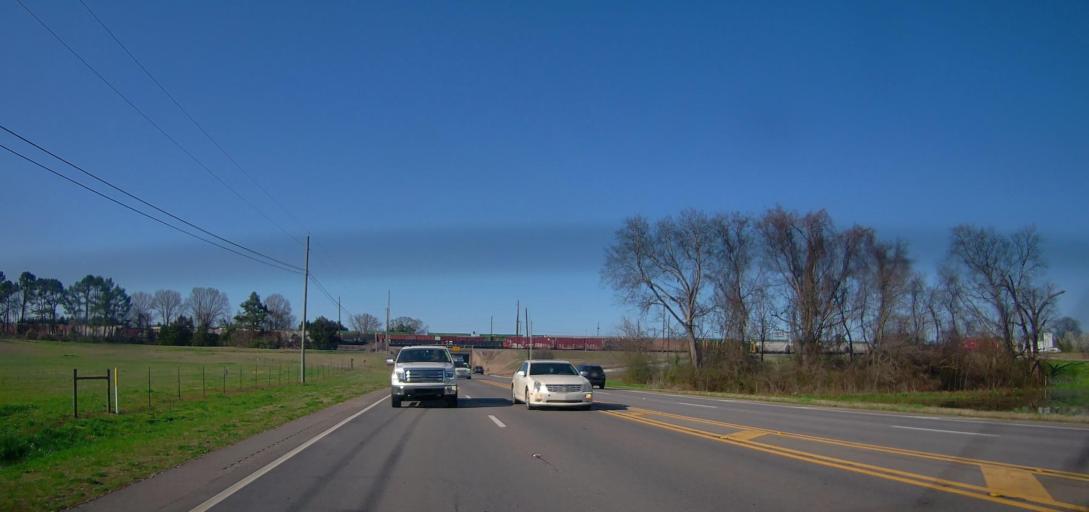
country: US
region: Alabama
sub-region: Colbert County
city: Muscle Shoals
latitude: 34.7119
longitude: -87.6349
